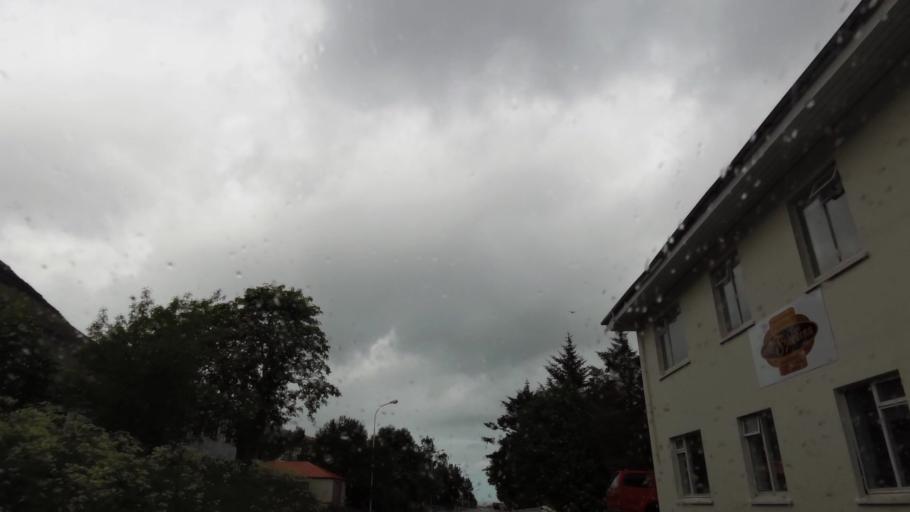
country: IS
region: Westfjords
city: Isafjoerdur
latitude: 65.8782
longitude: -23.4955
